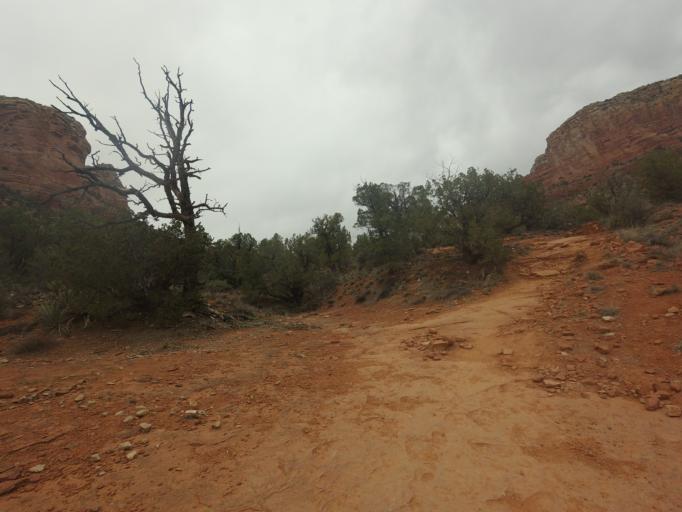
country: US
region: Arizona
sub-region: Yavapai County
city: Village of Oak Creek (Big Park)
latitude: 34.8015
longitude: -111.7469
